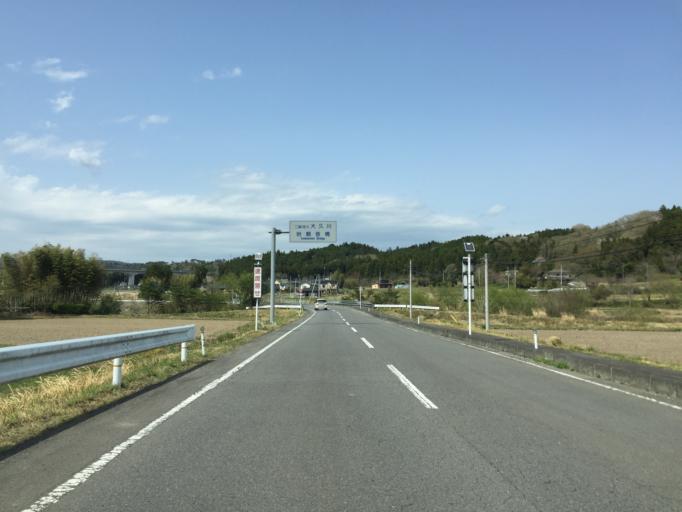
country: JP
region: Fukushima
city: Iwaki
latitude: 37.1635
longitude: 140.9721
